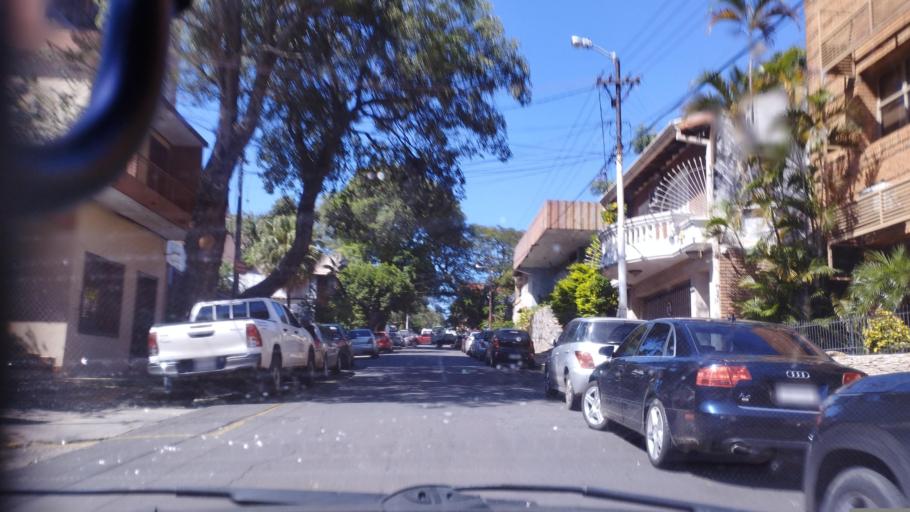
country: PY
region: Asuncion
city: Asuncion
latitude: -25.2895
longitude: -57.6438
